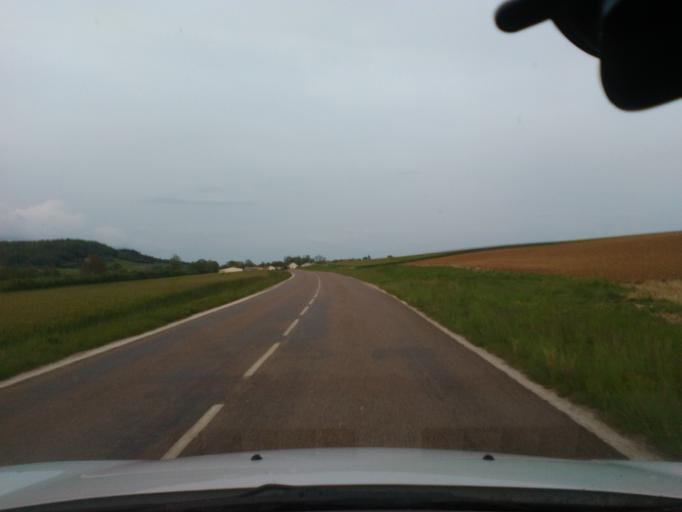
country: FR
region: Champagne-Ardenne
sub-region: Departement de la Haute-Marne
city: Bologne
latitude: 48.2155
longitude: 5.2339
